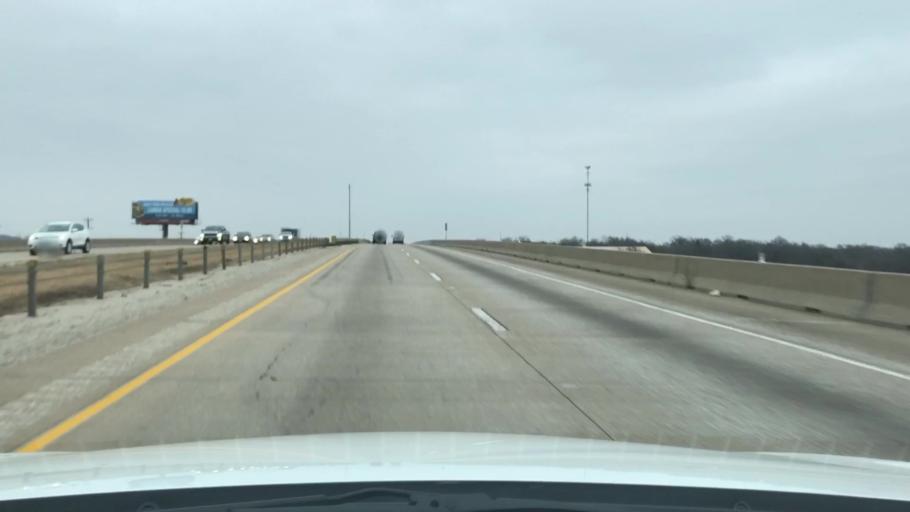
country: US
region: Texas
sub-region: Denton County
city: Sanger
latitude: 33.3129
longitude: -97.1793
